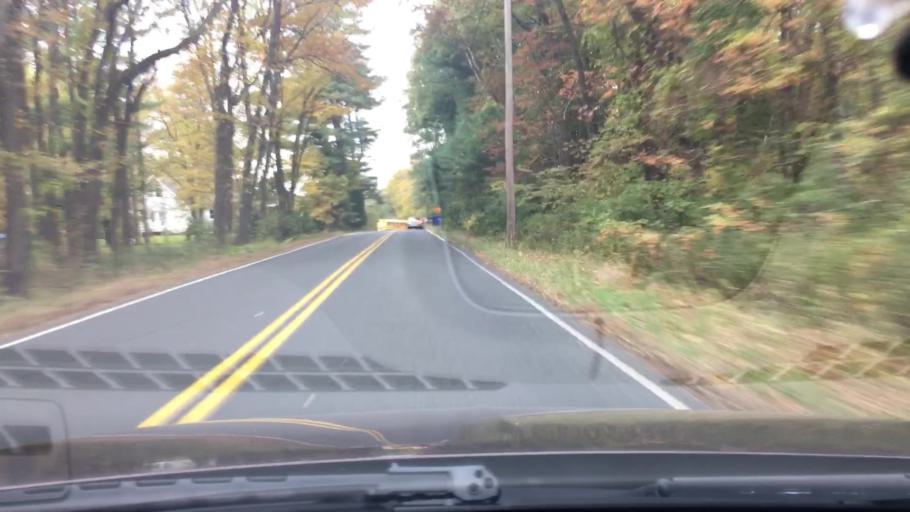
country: US
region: Connecticut
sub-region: Tolland County
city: Ellington
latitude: 41.9513
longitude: -72.4824
